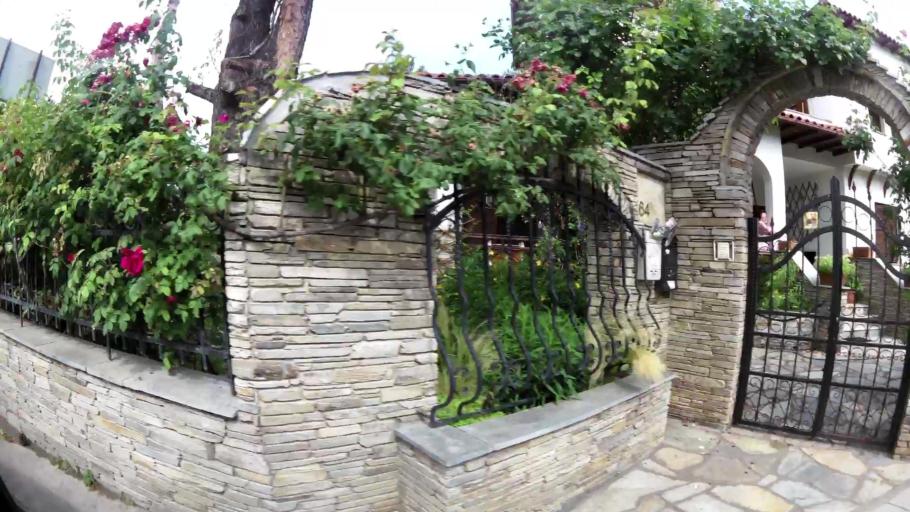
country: GR
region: Central Macedonia
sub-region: Nomos Thessalonikis
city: Panorama
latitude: 40.5831
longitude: 23.0198
